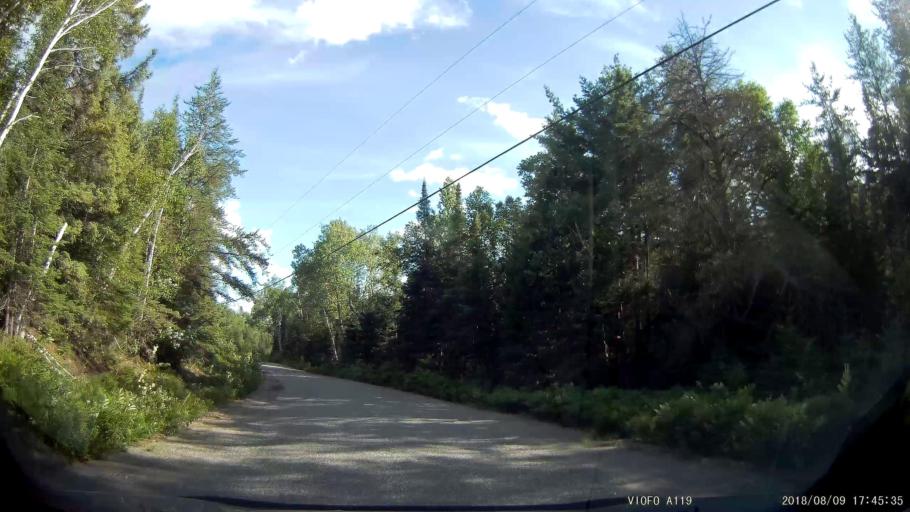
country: CA
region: Ontario
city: Rayside-Balfour
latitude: 46.5994
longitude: -81.5349
